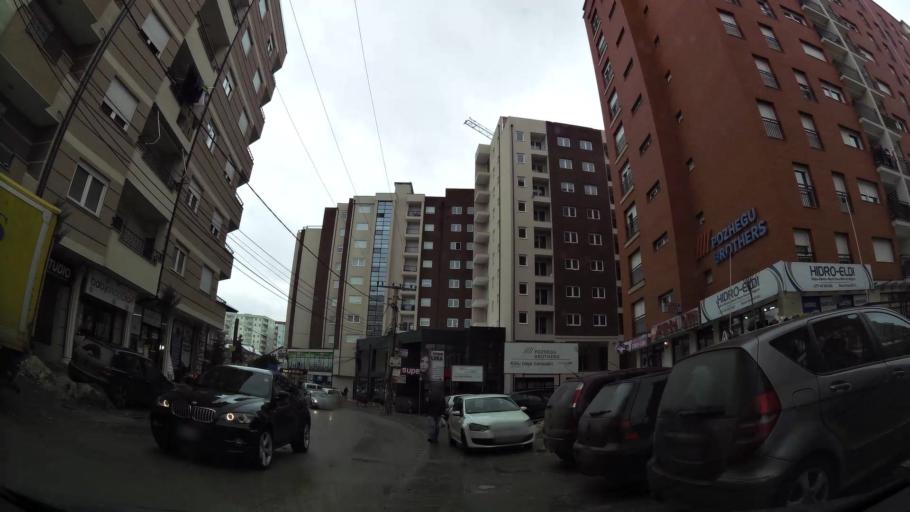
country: XK
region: Pristina
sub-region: Komuna e Prishtines
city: Pristina
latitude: 42.6456
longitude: 21.1749
